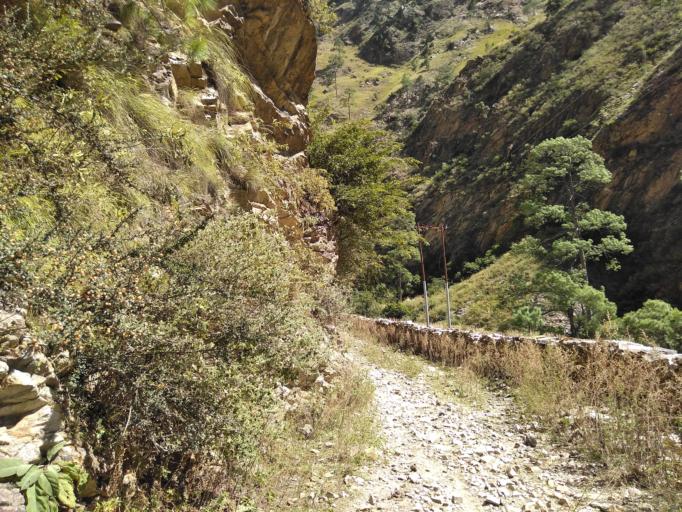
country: NP
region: Western Region
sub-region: Dhawalagiri Zone
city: Jomsom
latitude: 28.9370
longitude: 82.9325
